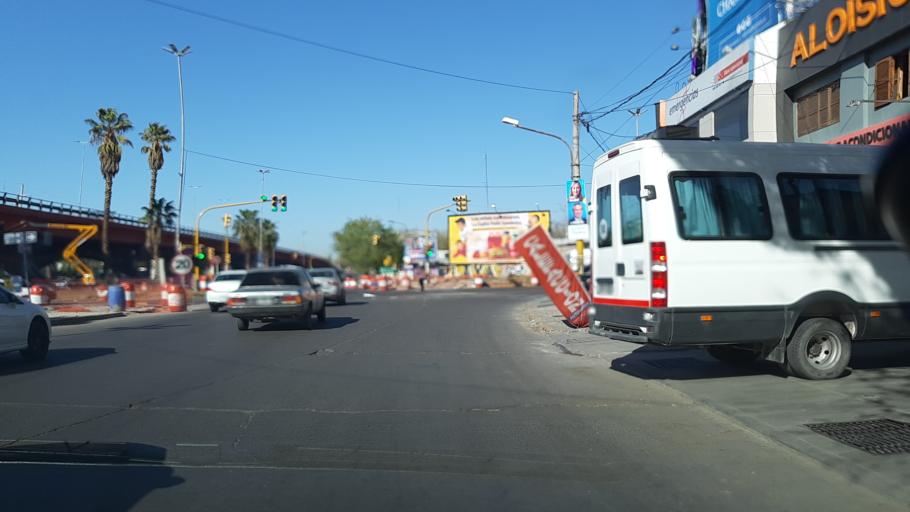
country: AR
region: Mendoza
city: Mendoza
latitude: -32.8958
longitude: -68.8333
